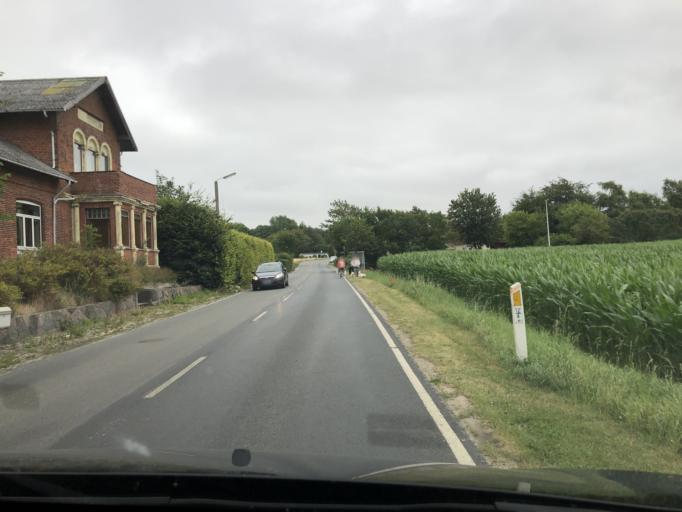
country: DK
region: South Denmark
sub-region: AEro Kommune
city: AEroskobing
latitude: 54.9144
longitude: 10.2842
